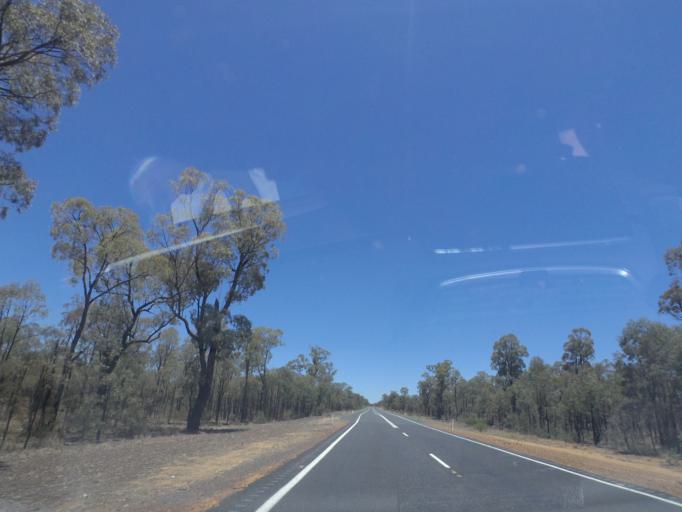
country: AU
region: New South Wales
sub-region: Warrumbungle Shire
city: Coonabarabran
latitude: -30.8661
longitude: 149.4521
